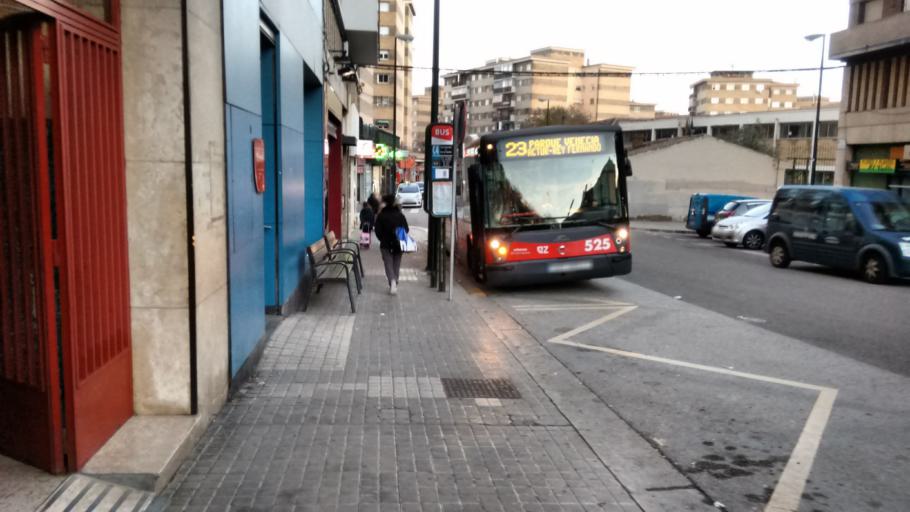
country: ES
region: Aragon
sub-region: Provincia de Zaragoza
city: Zaragoza
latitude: 41.6258
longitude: -0.8780
